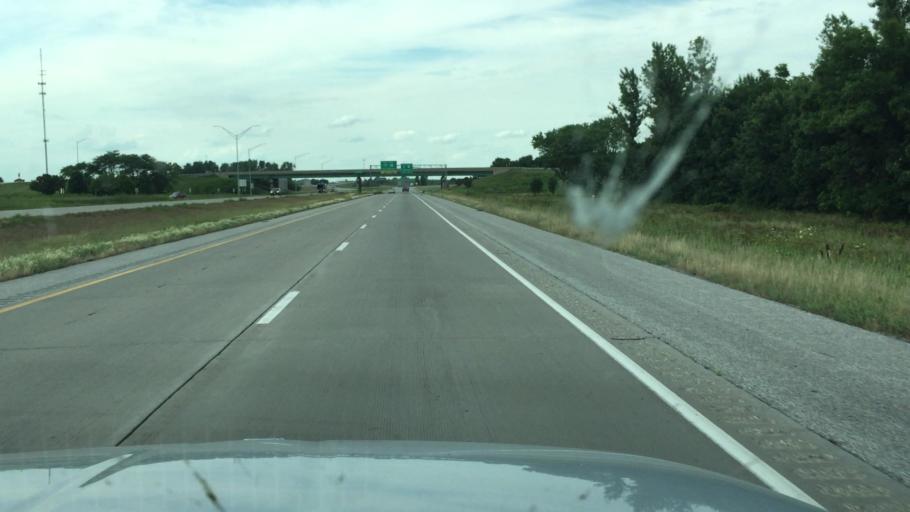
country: US
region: Iowa
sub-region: Scott County
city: Walcott
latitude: 41.5890
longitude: -90.6757
